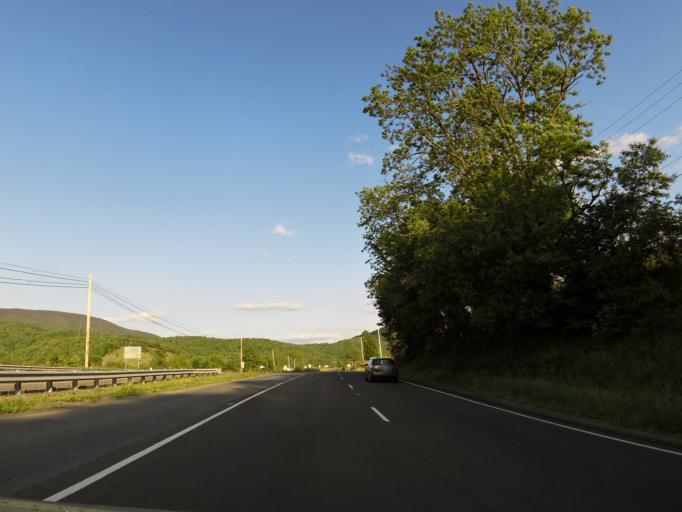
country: US
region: Virginia
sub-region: Russell County
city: Lebanon
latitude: 36.8228
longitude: -82.1403
